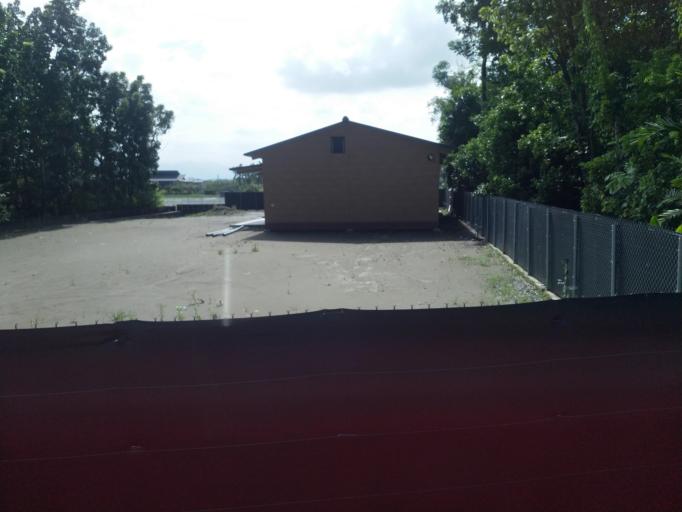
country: TW
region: Taiwan
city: Yujing
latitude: 22.9020
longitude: 120.5175
